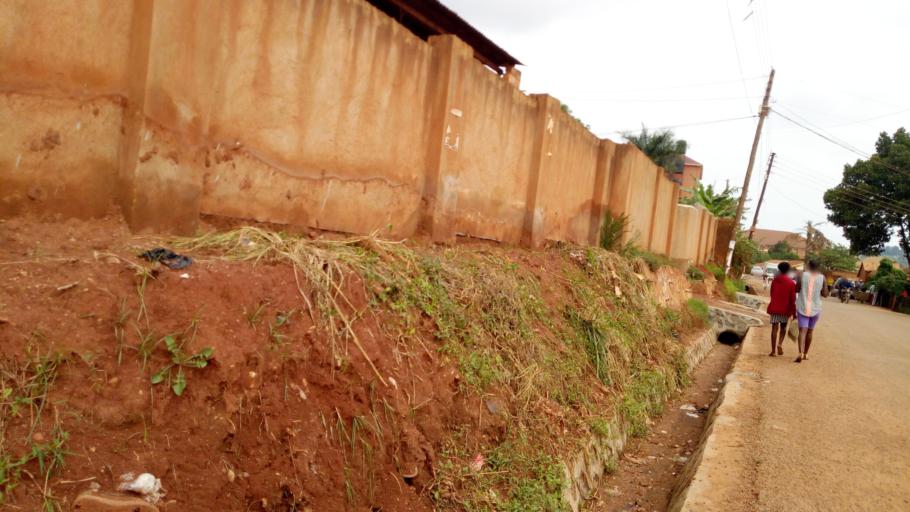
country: UG
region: Central Region
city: Kampala Central Division
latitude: 0.3387
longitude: 32.5612
